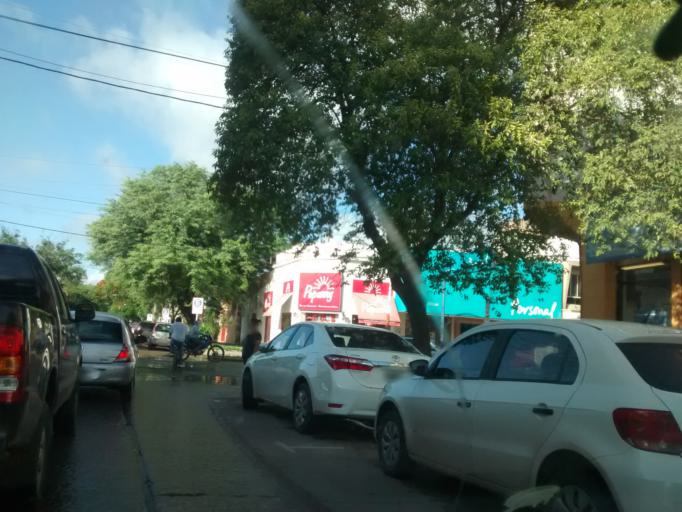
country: AR
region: Chaco
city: Resistencia
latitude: -27.4556
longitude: -58.9846
